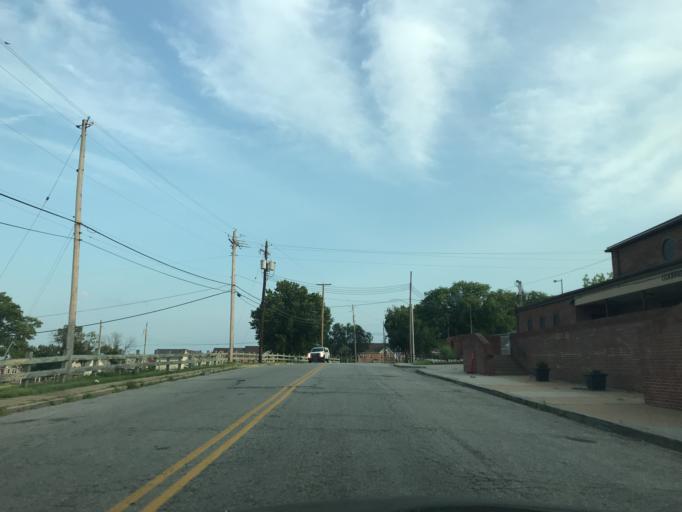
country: US
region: Maryland
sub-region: Baltimore County
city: Dundalk
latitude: 39.2799
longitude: -76.5404
